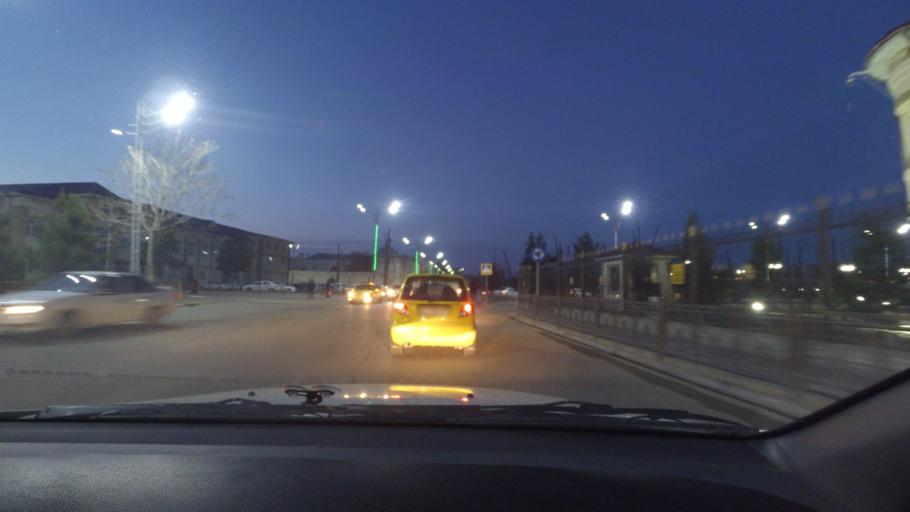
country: UZ
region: Bukhara
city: Bukhara
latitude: 39.7753
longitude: 64.4071
